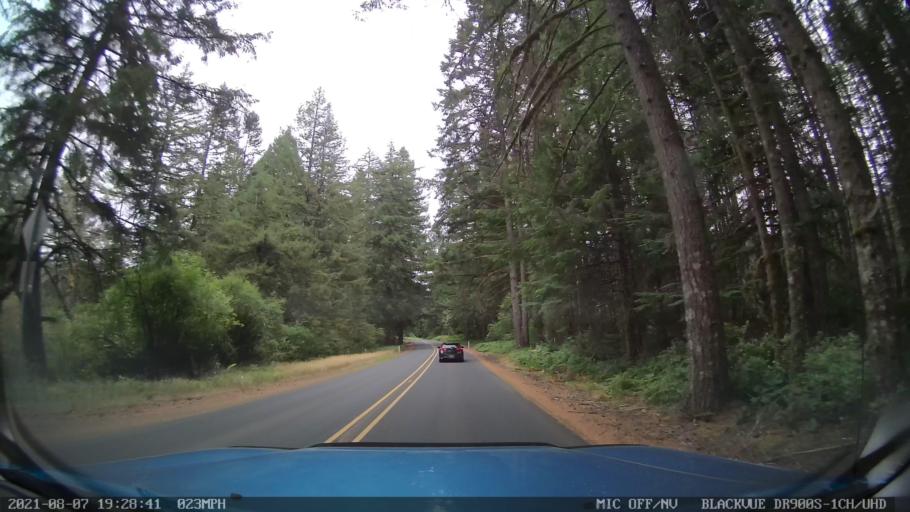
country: US
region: Oregon
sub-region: Linn County
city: Lyons
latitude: 44.8845
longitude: -122.6377
